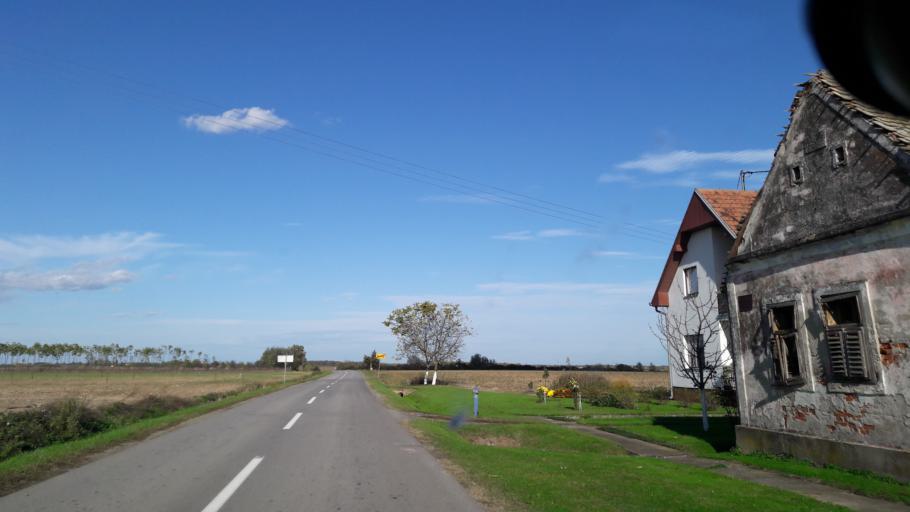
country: HR
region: Osjecko-Baranjska
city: Gorjani
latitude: 45.3846
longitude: 18.2836
